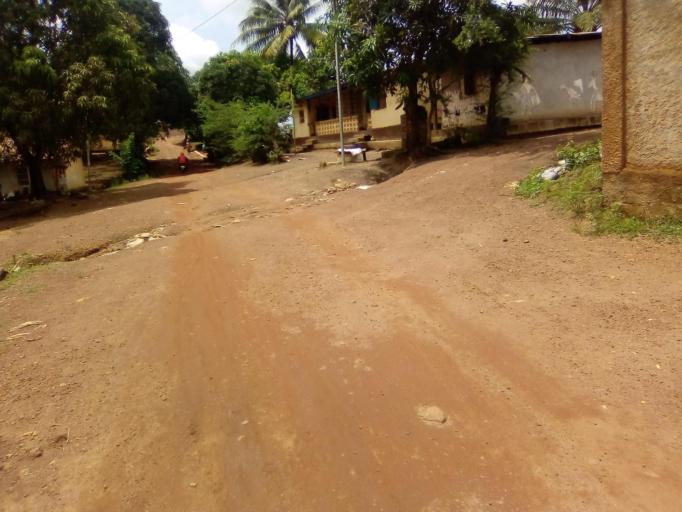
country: SL
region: Southern Province
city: Bo
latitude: 7.9323
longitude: -11.7227
